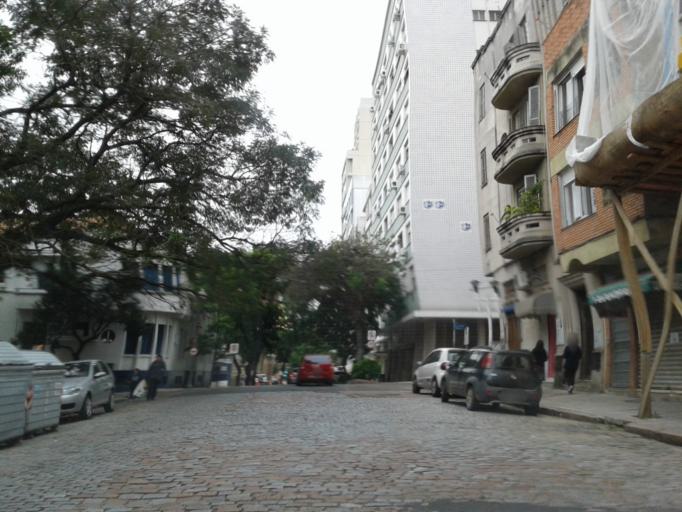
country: BR
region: Rio Grande do Sul
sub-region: Porto Alegre
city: Porto Alegre
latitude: -30.0326
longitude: -51.2378
